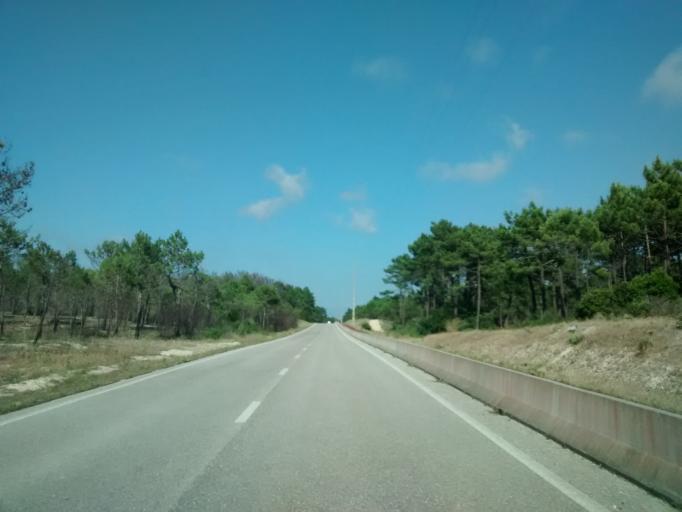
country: PT
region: Coimbra
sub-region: Figueira da Foz
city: Lavos
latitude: 40.0008
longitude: -8.8984
